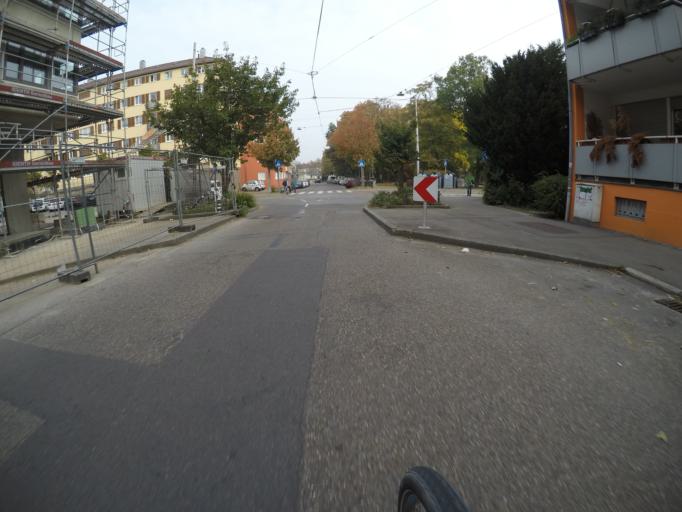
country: DE
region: Baden-Wuerttemberg
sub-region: Regierungsbezirk Stuttgart
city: Stuttgart-Ost
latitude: 48.7806
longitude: 9.2095
